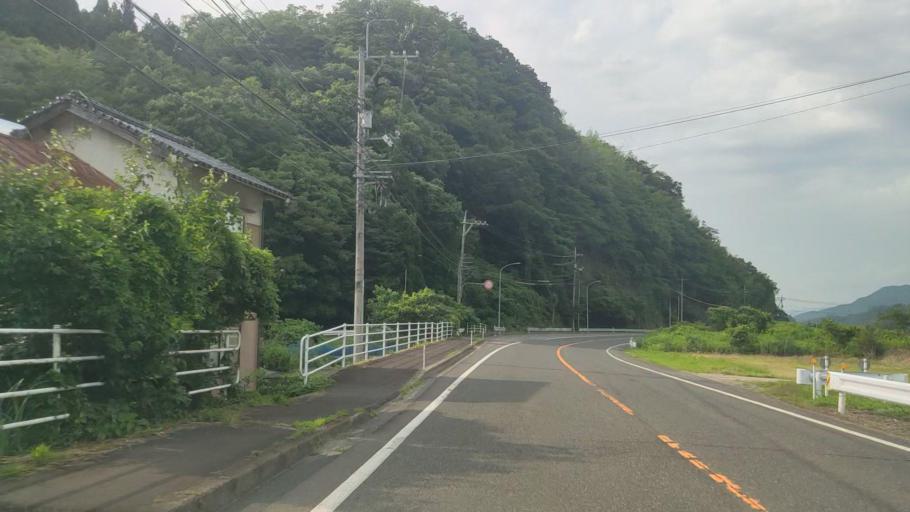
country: JP
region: Tottori
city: Kurayoshi
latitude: 35.3396
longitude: 133.8402
